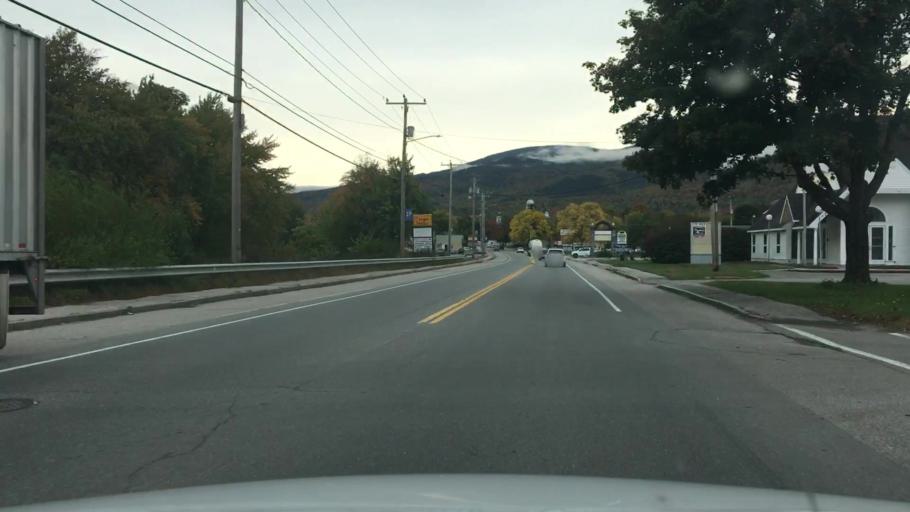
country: US
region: New Hampshire
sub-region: Coos County
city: Gorham
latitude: 44.3914
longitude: -71.1842
